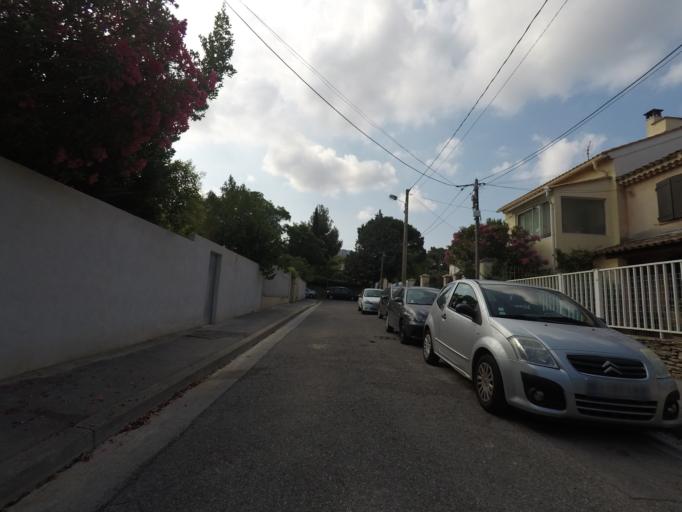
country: FR
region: Provence-Alpes-Cote d'Azur
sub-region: Departement des Bouches-du-Rhone
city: Marseille 09
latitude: 43.2588
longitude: 5.4207
